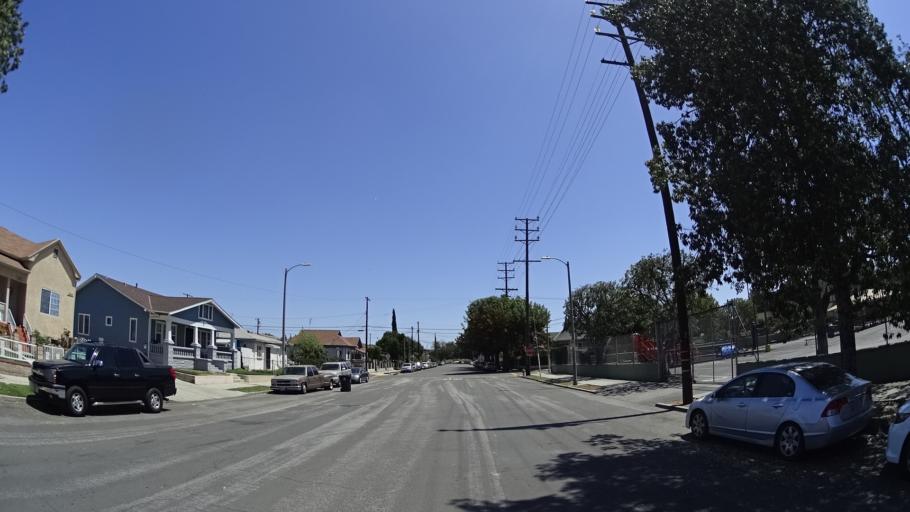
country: US
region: California
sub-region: Los Angeles County
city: Los Angeles
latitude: 34.0674
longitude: -118.2201
